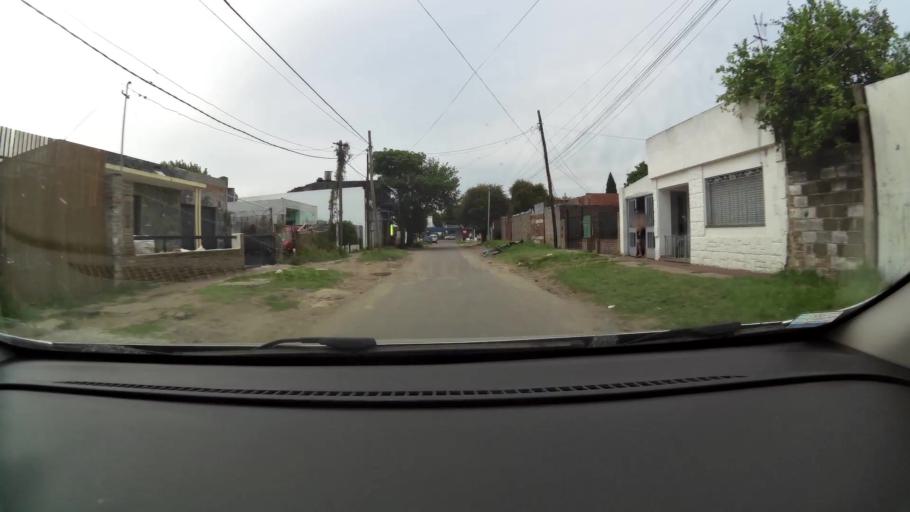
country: AR
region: Santa Fe
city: Granadero Baigorria
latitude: -32.8948
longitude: -60.7096
